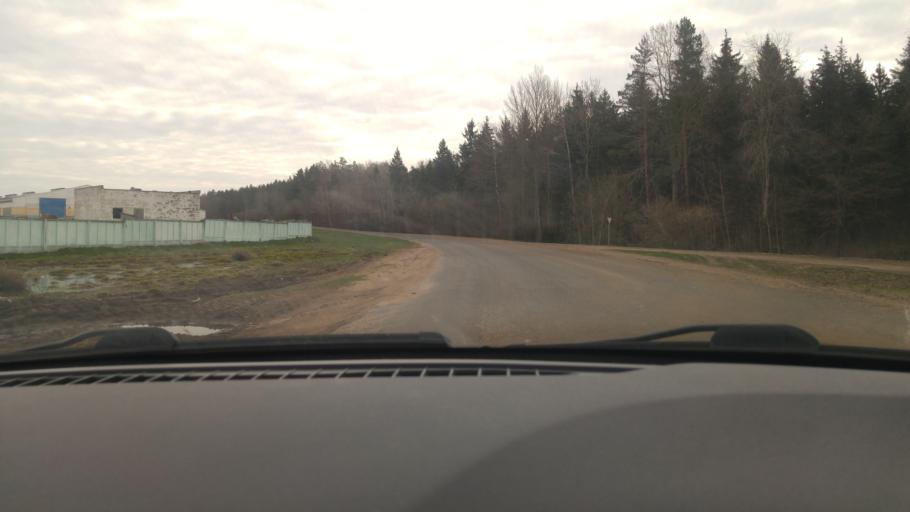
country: BY
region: Minsk
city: Chervyen'
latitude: 53.6896
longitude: 28.4454
